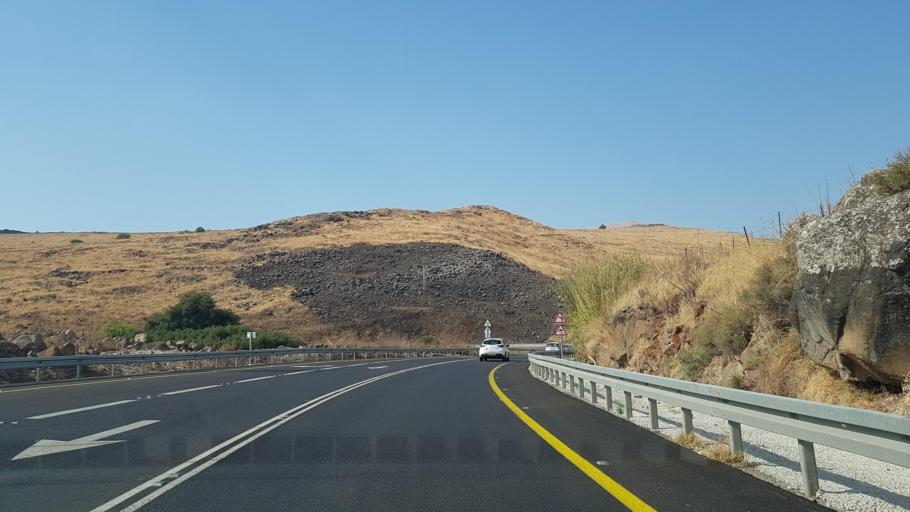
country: IL
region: Northern District
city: Rosh Pinna
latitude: 32.9126
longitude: 35.5651
